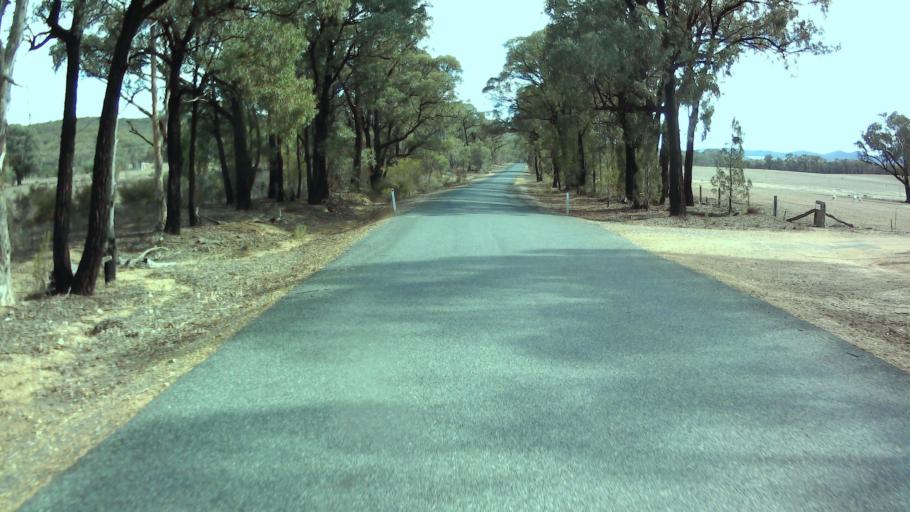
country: AU
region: New South Wales
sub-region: Weddin
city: Grenfell
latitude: -33.8766
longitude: 148.2013
